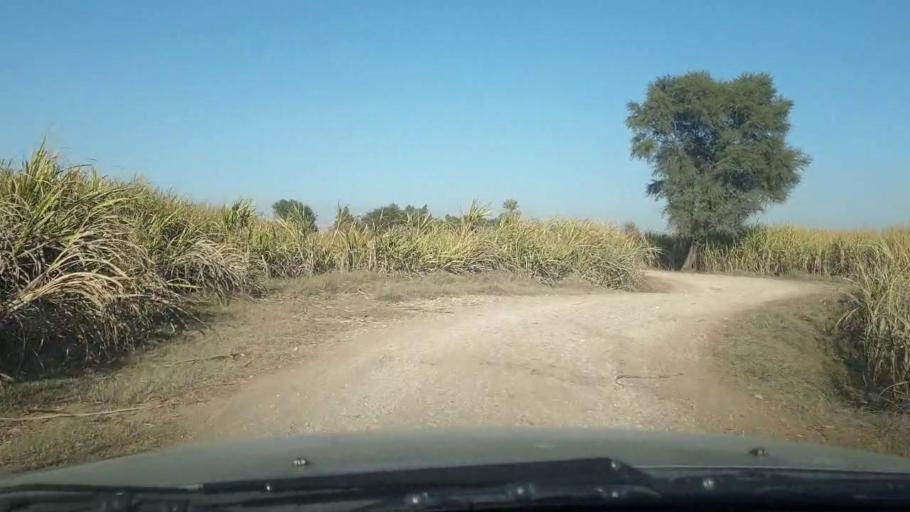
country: PK
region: Sindh
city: Adilpur
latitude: 27.9588
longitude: 69.2014
